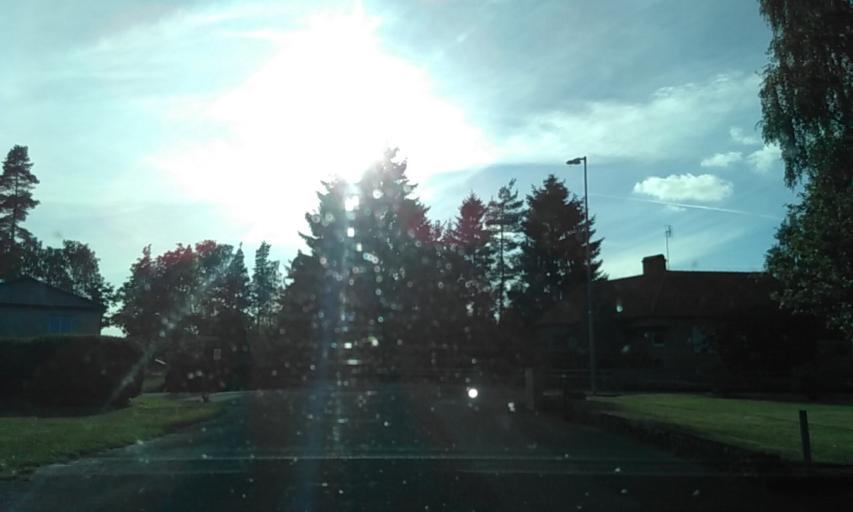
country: SE
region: Vaestra Goetaland
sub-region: Vara Kommun
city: Vara
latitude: 58.3274
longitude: 12.9202
